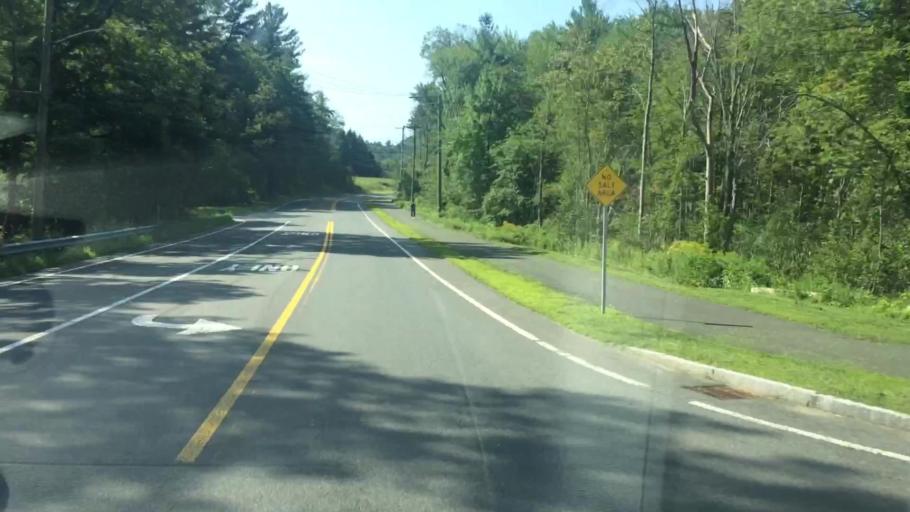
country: US
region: Massachusetts
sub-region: Hampshire County
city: South Amherst
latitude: 42.3233
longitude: -72.5248
